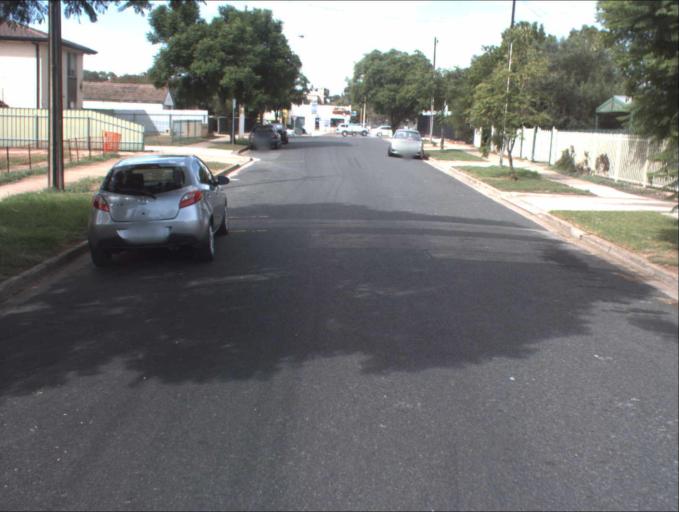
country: AU
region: South Australia
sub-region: Port Adelaide Enfield
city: Blair Athol
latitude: -34.8636
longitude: 138.6001
